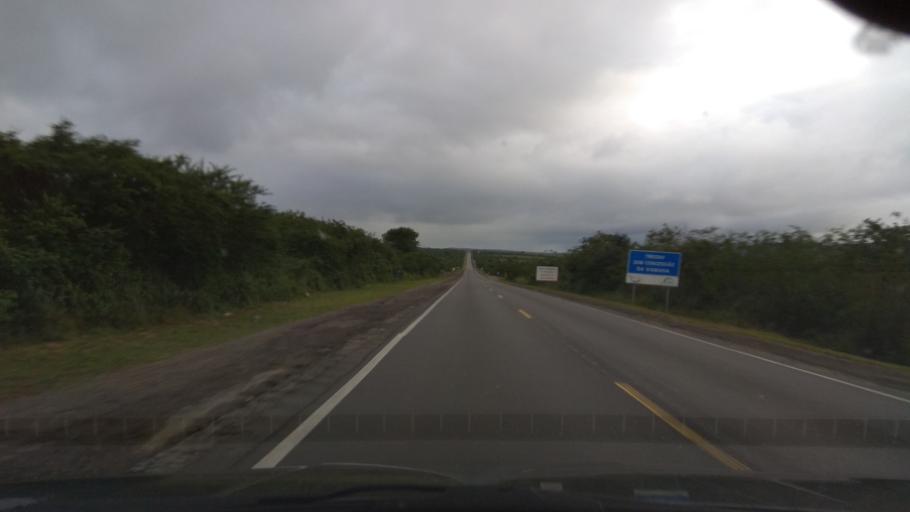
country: BR
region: Bahia
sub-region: Jaguaquara
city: Jaguaquara
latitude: -13.4065
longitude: -40.0248
